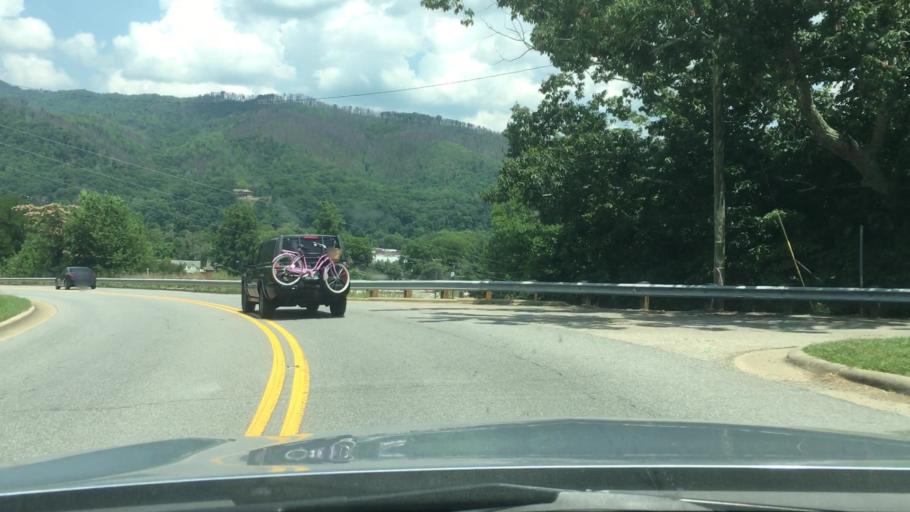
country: US
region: North Carolina
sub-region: Madison County
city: Marshall
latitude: 35.8911
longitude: -82.8318
